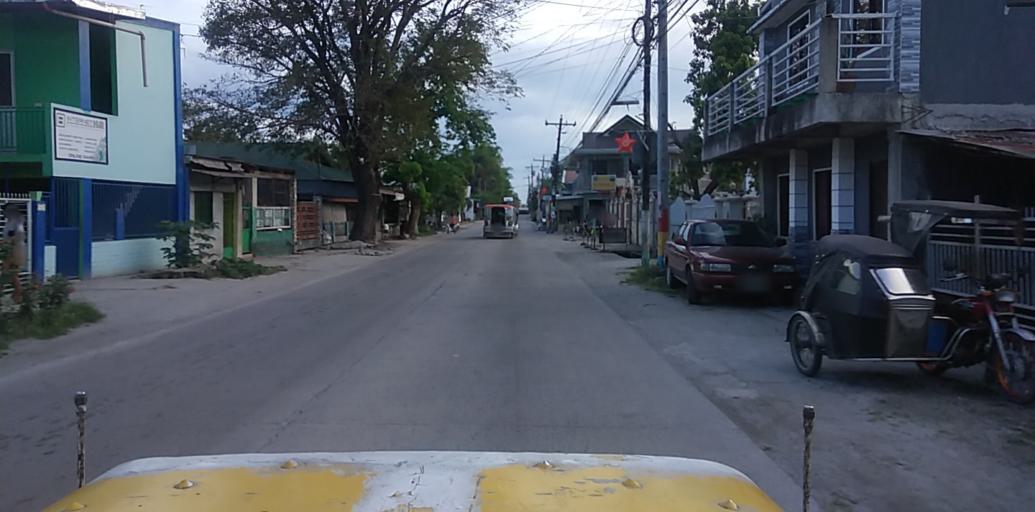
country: PH
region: Central Luzon
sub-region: Province of Pampanga
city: San Antonio
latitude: 15.1532
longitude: 120.6883
